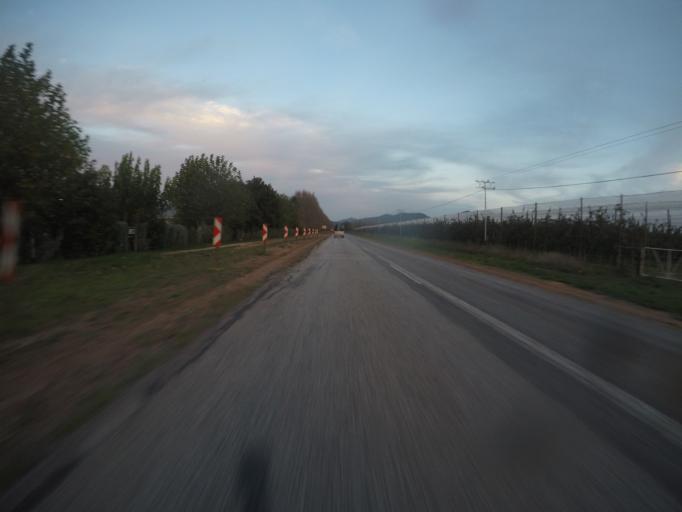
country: ZA
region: Western Cape
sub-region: Eden District Municipality
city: Plettenberg Bay
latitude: -33.7507
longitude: 23.4834
